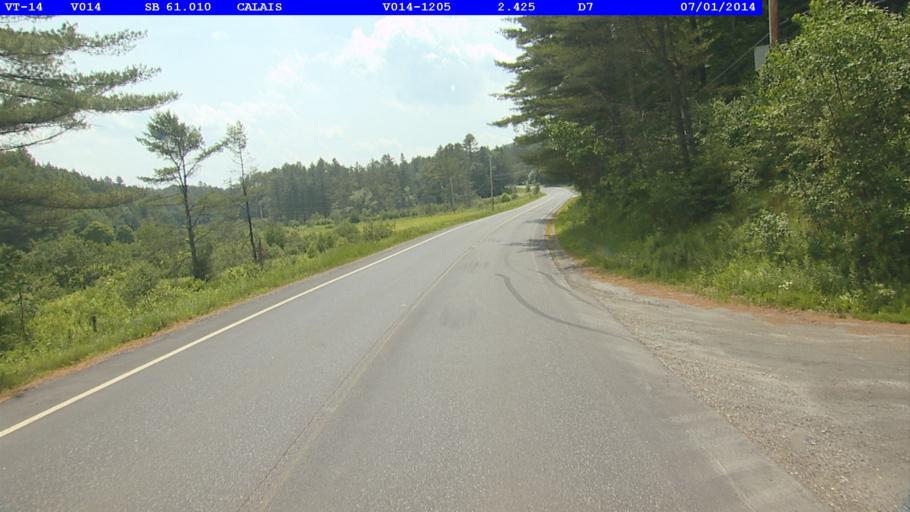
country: US
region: Vermont
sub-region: Washington County
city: Montpelier
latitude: 44.3412
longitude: -72.4434
